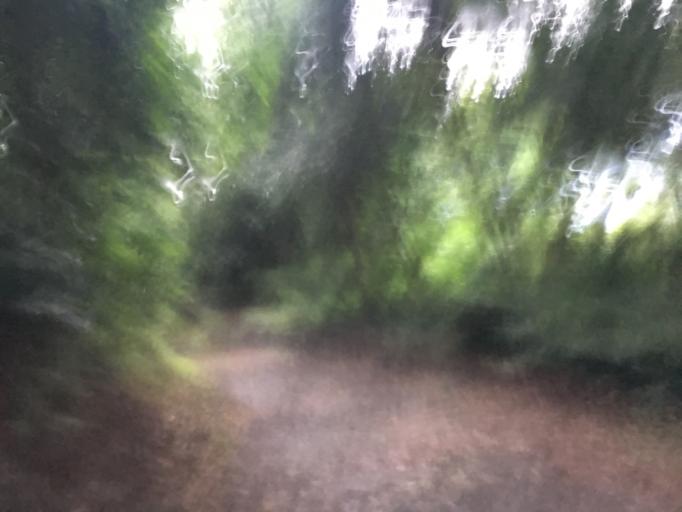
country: JP
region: Aichi
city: Ishiki
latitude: 34.7301
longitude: 137.0437
